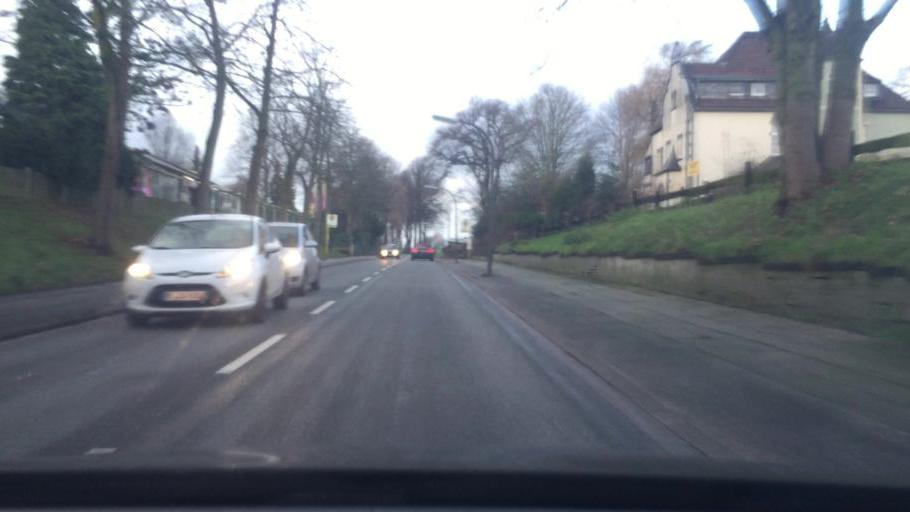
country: DE
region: North Rhine-Westphalia
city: Oer-Erkenschwick
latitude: 51.6131
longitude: 7.2600
